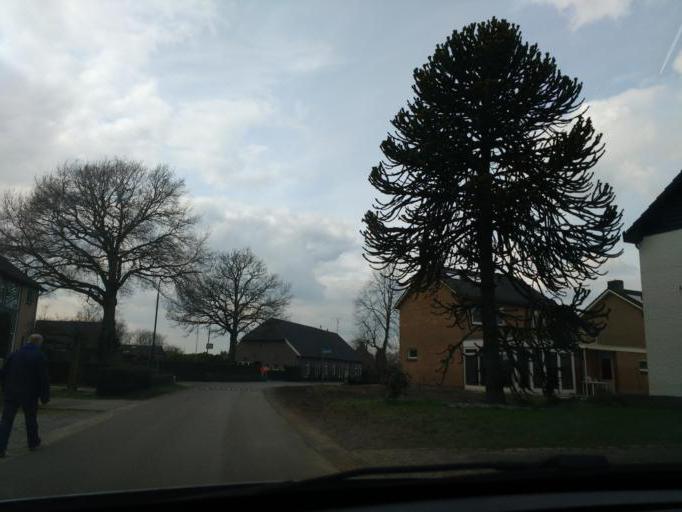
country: NL
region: Limburg
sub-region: Gemeente Venray
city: Venray
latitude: 51.5733
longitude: 6.0067
